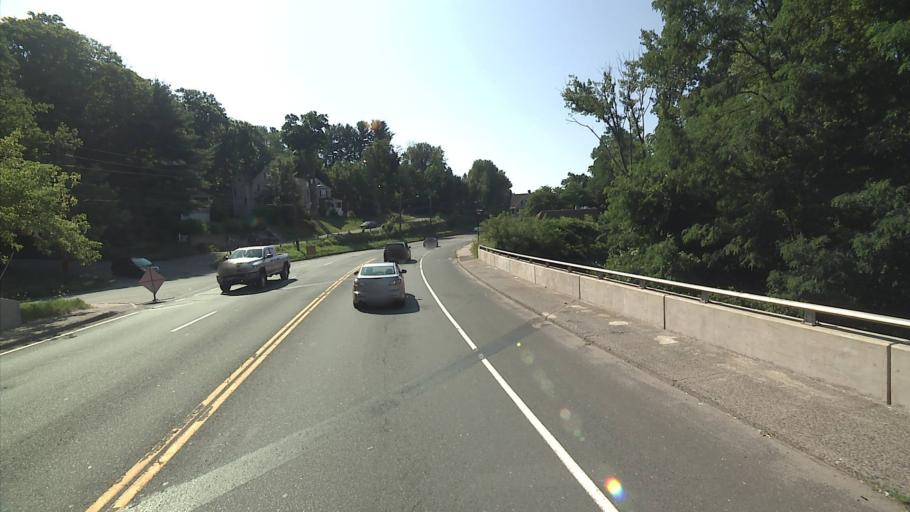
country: US
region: Connecticut
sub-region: Litchfield County
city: Winsted
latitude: 41.9194
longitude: -73.0579
